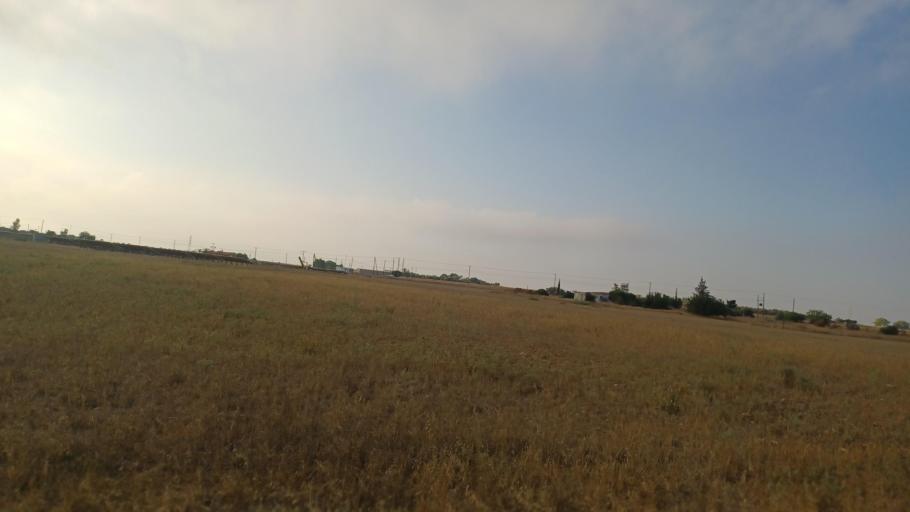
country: CY
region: Ammochostos
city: Avgorou
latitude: 35.0426
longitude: 33.8520
